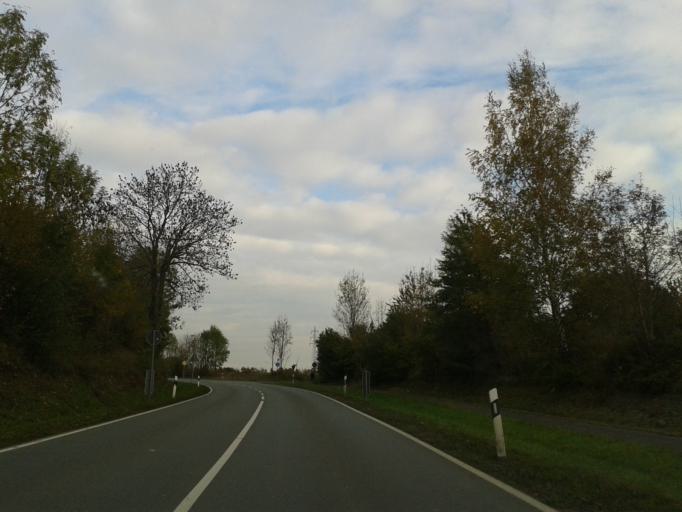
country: DE
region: North Rhine-Westphalia
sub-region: Regierungsbezirk Detmold
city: Horn
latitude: 51.8720
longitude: 8.9567
